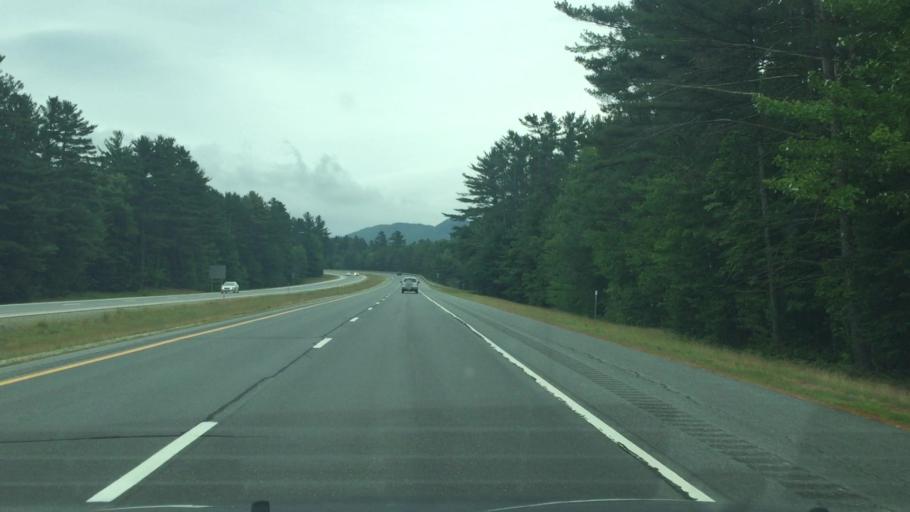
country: US
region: New Hampshire
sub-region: Grafton County
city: Littleton
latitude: 44.2134
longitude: -71.7251
